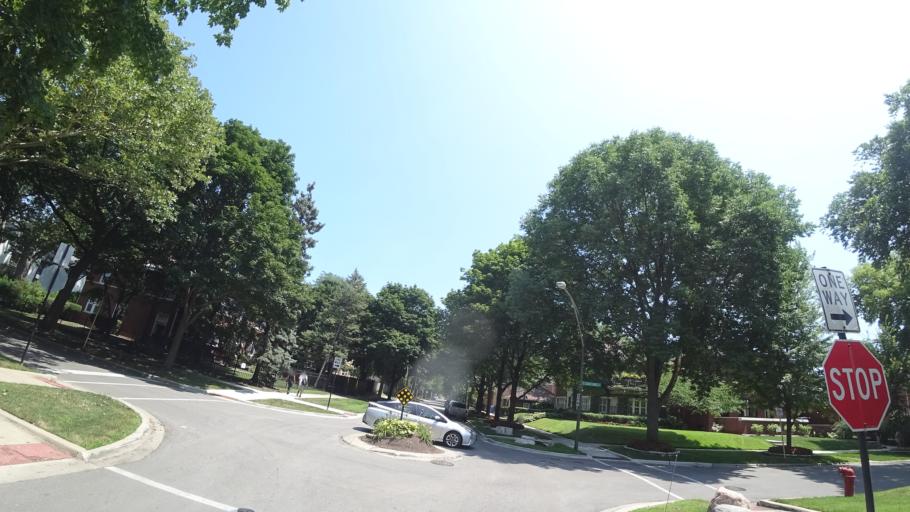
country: US
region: Illinois
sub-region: Cook County
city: Chicago
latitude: 41.7698
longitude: -87.5803
